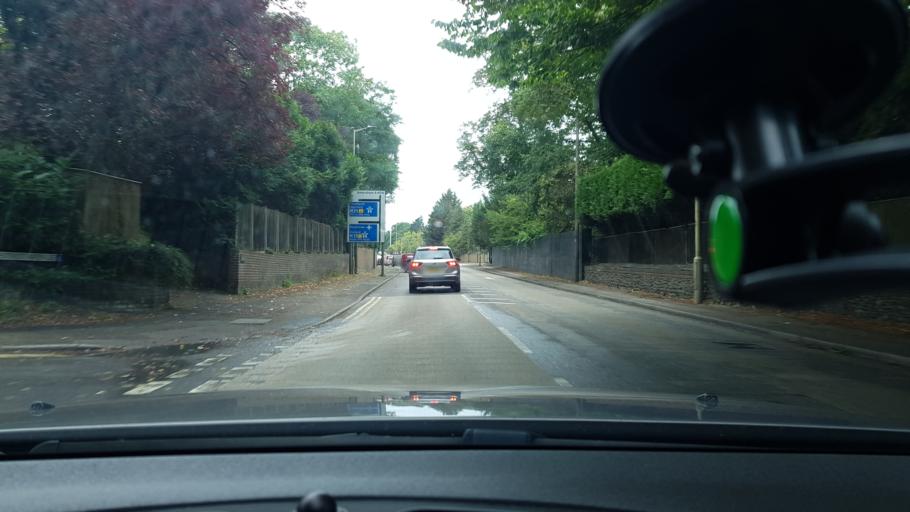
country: GB
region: England
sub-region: Hertfordshire
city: Chorleywood
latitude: 51.6545
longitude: -0.4913
